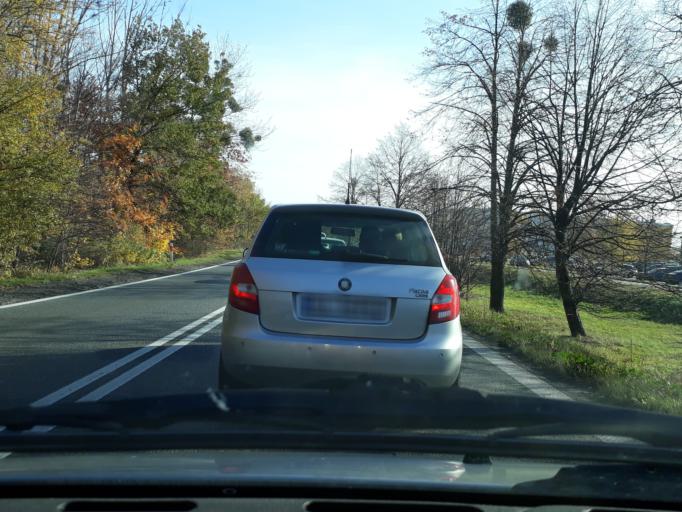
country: PL
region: Silesian Voivodeship
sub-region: Powiat tarnogorski
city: Tarnowskie Gory
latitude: 50.4400
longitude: 18.8374
